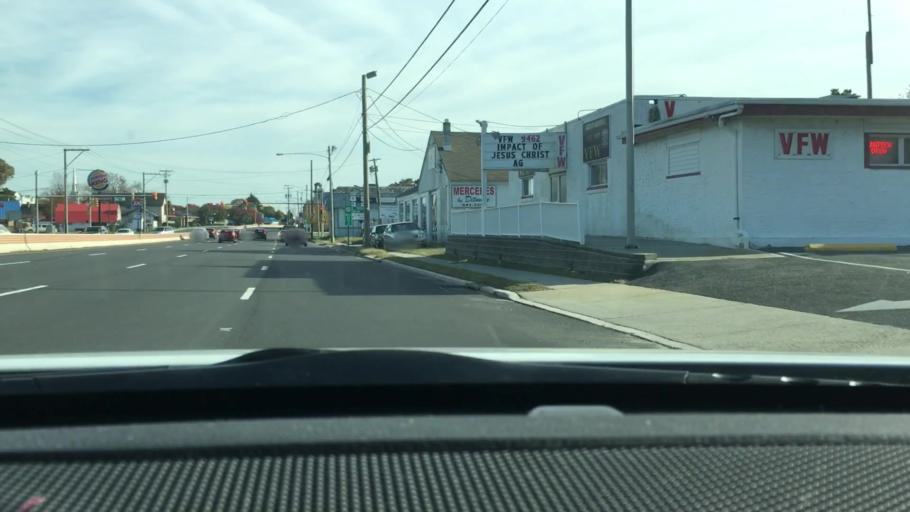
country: US
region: New Jersey
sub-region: Atlantic County
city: Absecon
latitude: 39.4288
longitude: -74.5069
